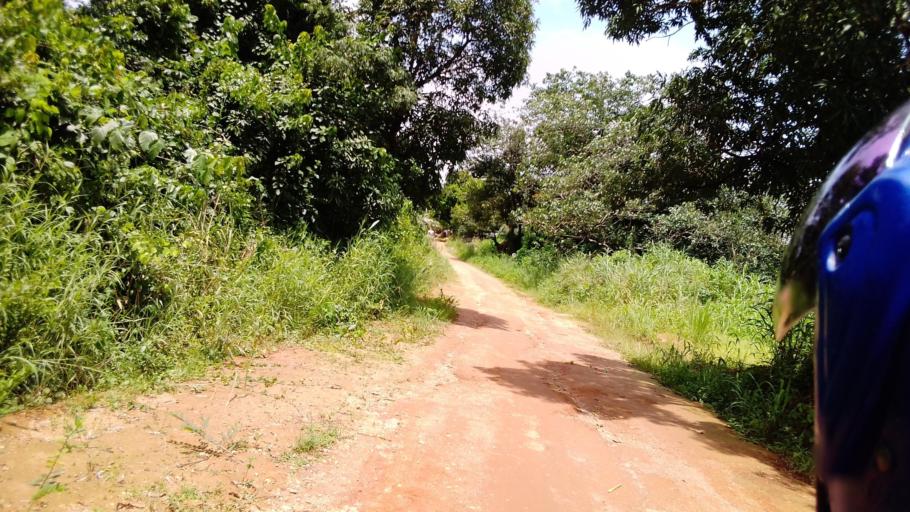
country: SL
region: Eastern Province
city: Koidu
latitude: 8.6653
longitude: -10.9429
